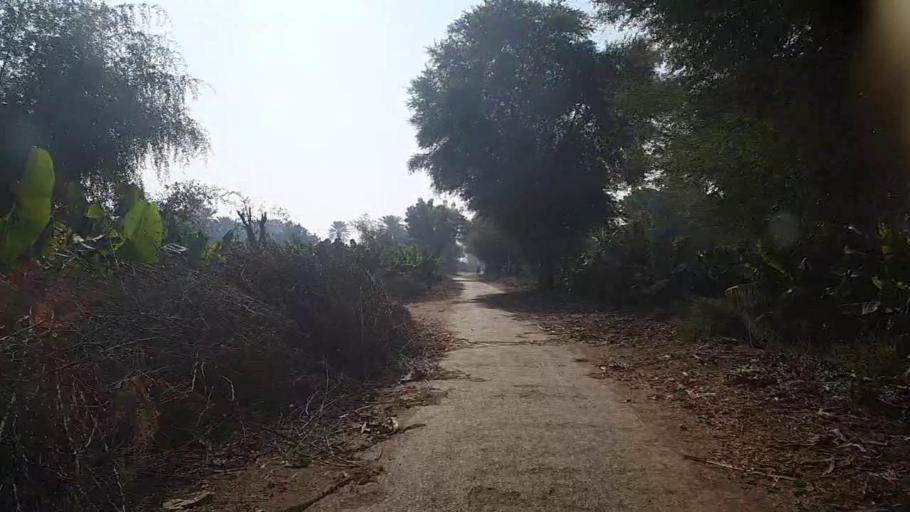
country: PK
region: Sindh
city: Kandiari
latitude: 27.0157
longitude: 68.5018
